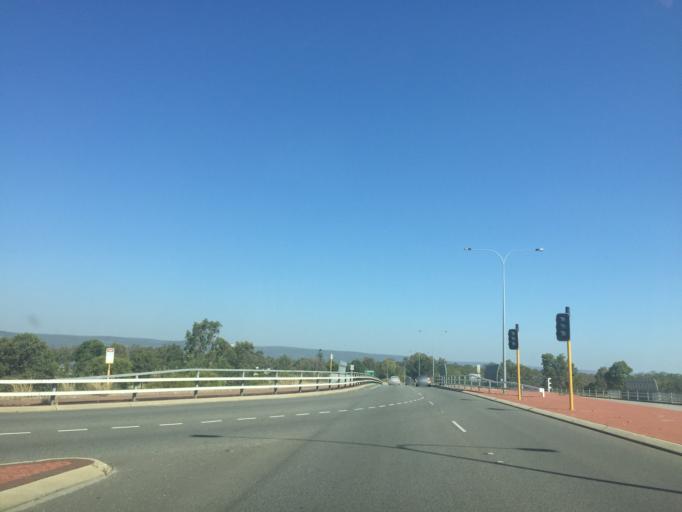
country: AU
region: Western Australia
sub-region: Gosnells
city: Kenwick
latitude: -32.0374
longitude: 115.9604
